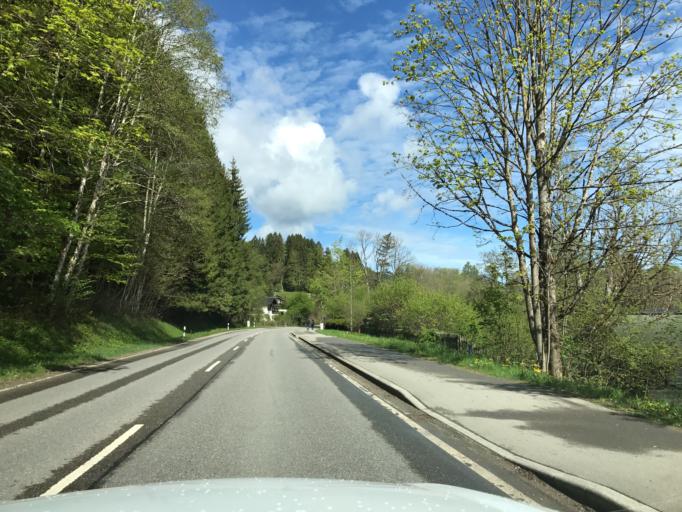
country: DE
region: Bavaria
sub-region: Upper Bavaria
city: Bad Wiessee
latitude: 47.6945
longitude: 11.7339
